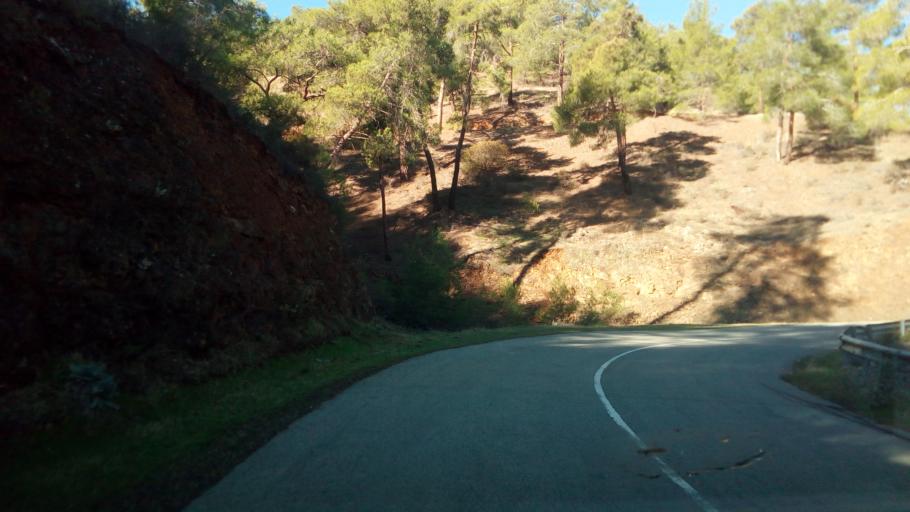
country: CY
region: Lefkosia
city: Lefka
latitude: 35.0805
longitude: 32.8019
